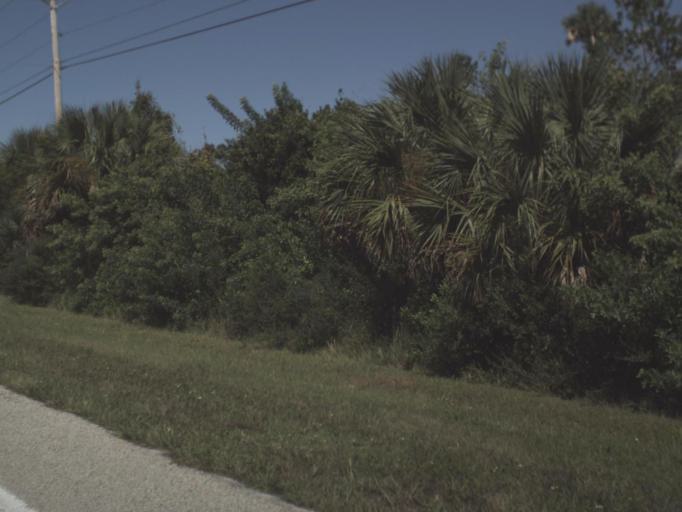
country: US
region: Florida
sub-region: Collier County
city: Marco
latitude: 25.9425
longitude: -81.4716
